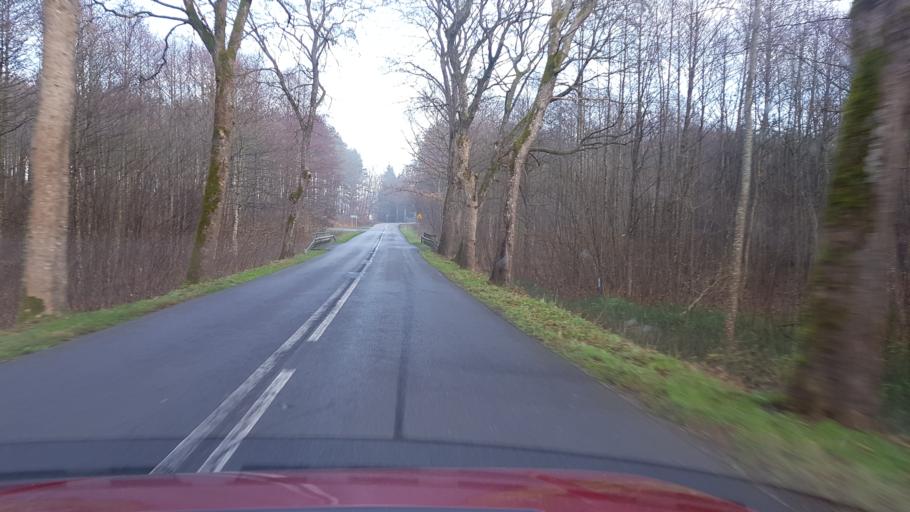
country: PL
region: West Pomeranian Voivodeship
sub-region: Powiat bialogardzki
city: Tychowo
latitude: 53.9445
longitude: 16.3180
